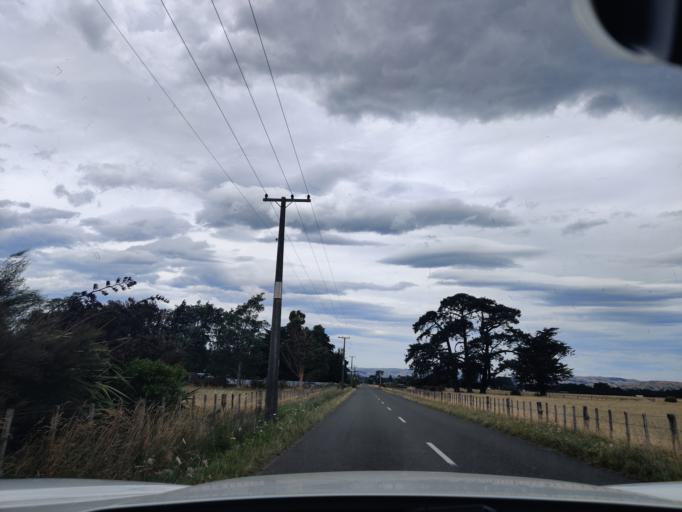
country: NZ
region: Wellington
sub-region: Masterton District
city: Masterton
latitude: -41.0191
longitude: 175.4663
